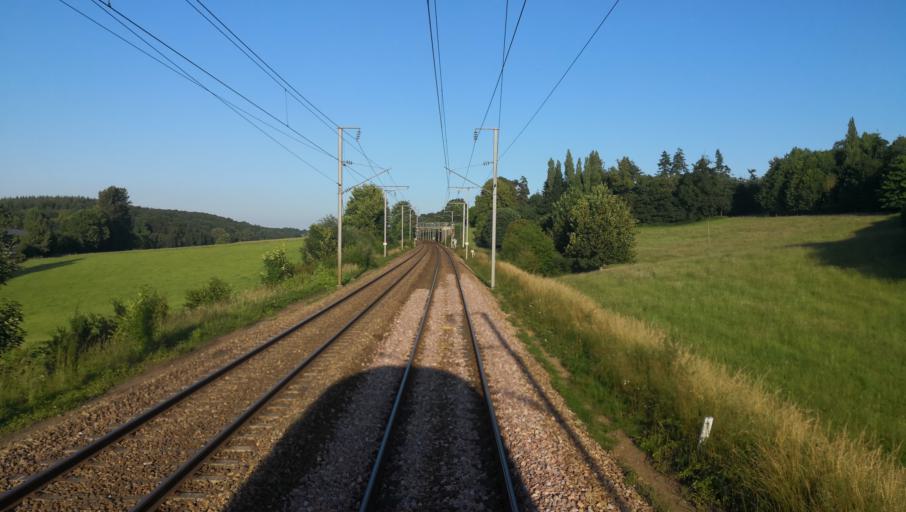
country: FR
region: Lower Normandy
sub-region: Departement du Calvados
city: La Vespiere
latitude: 49.0791
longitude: 0.3777
